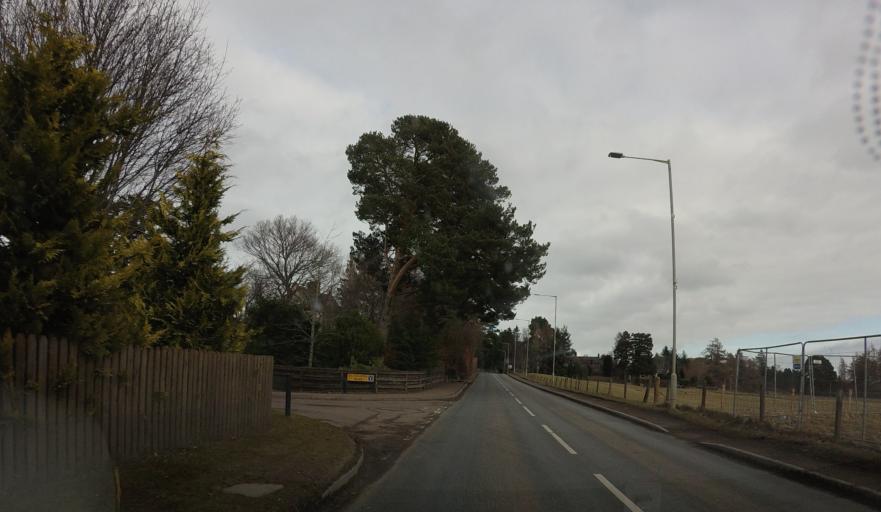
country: GB
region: Scotland
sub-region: Highland
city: Kingussie
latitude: 57.0607
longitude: -4.1272
